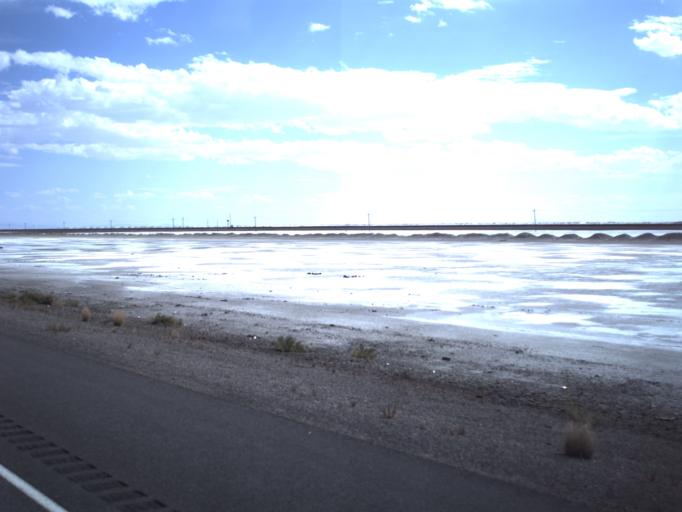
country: US
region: Utah
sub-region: Tooele County
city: Wendover
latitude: 40.7397
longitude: -113.9157
